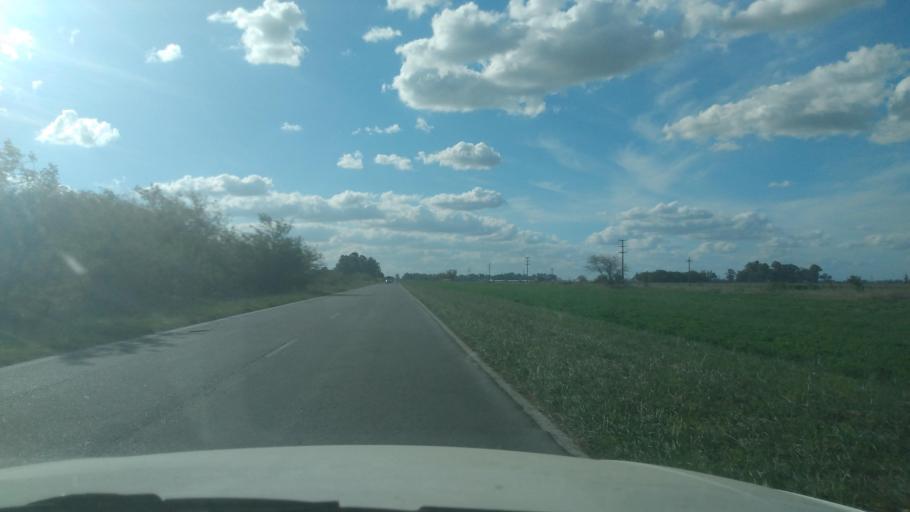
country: AR
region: Buenos Aires
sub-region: Partido de Navarro
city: Navarro
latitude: -34.9108
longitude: -59.3309
